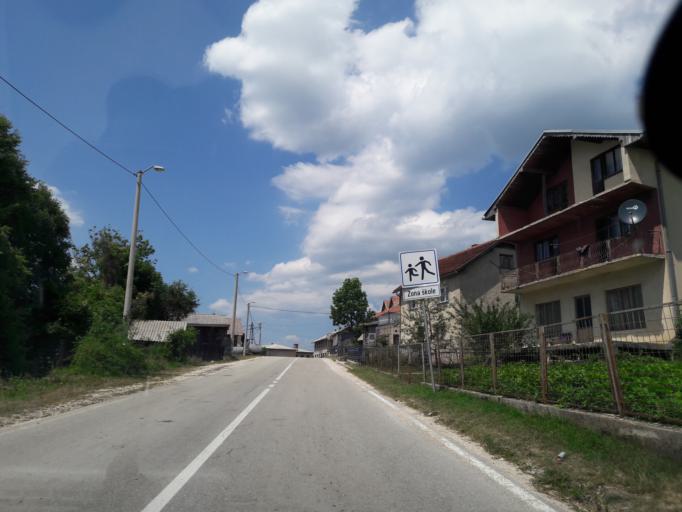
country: BA
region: Republika Srpska
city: Sipovo
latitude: 44.1771
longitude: 17.1633
